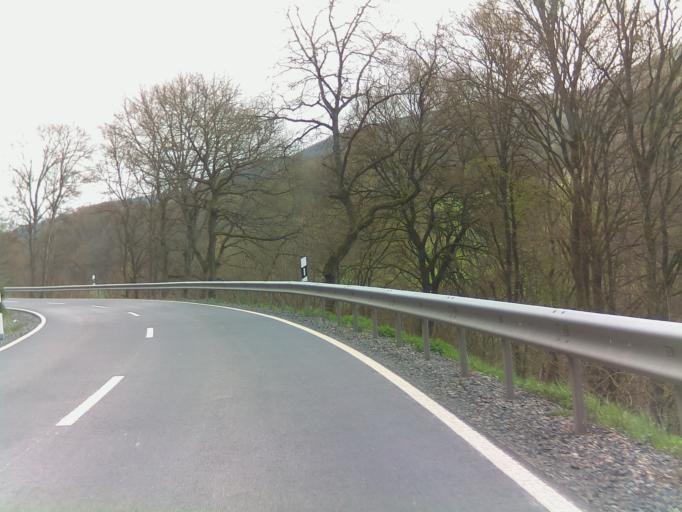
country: DE
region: Rheinland-Pfalz
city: Bruschied
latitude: 49.8210
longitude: 7.3981
